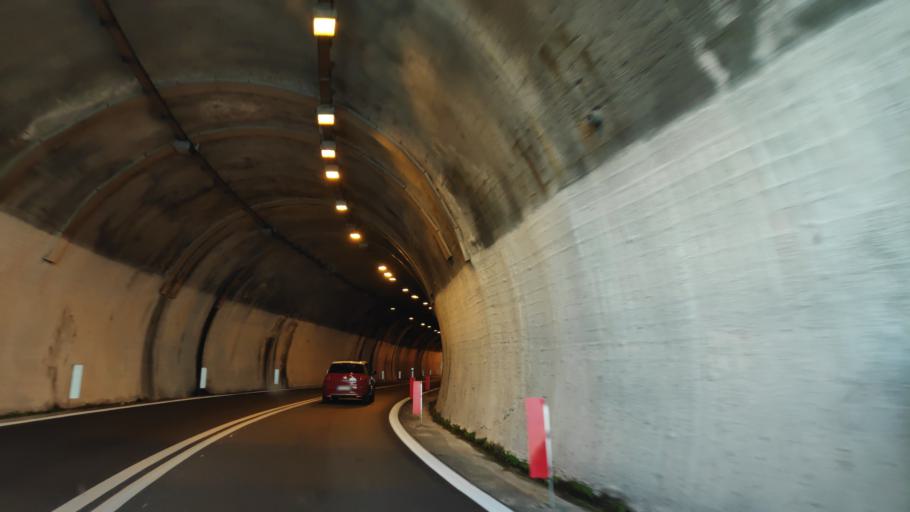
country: IT
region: Calabria
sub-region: Provincia di Reggio Calabria
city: Scilla
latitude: 38.2519
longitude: 15.7284
